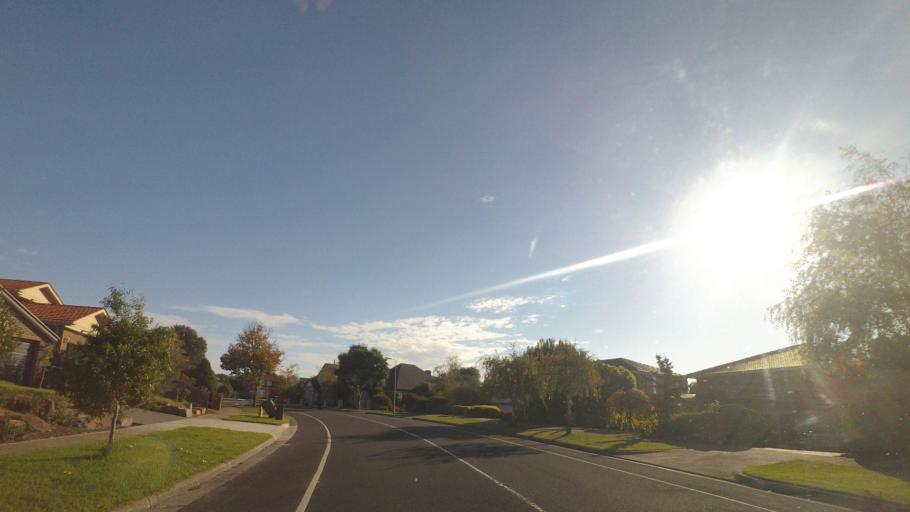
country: AU
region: Victoria
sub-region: Manningham
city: Doncaster East
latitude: -37.7644
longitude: 145.1591
